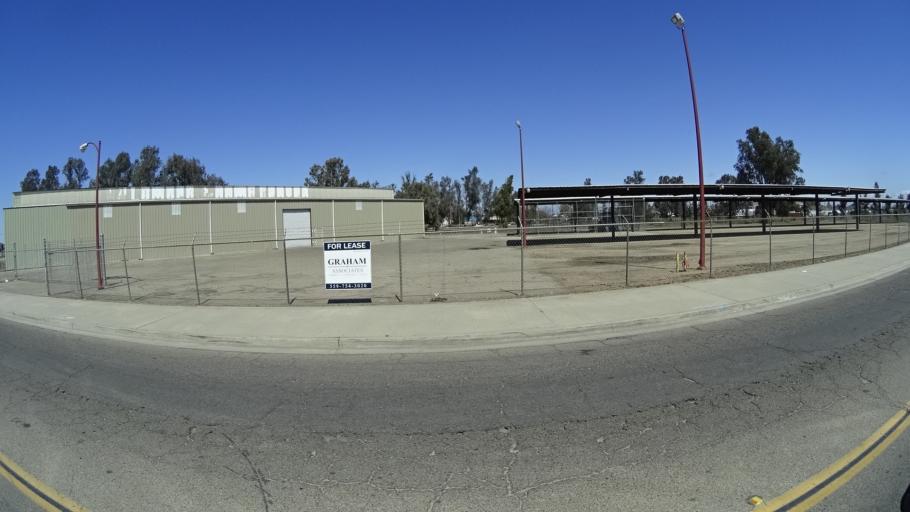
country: US
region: California
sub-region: Fresno County
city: West Park
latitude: 36.7922
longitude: -119.8658
